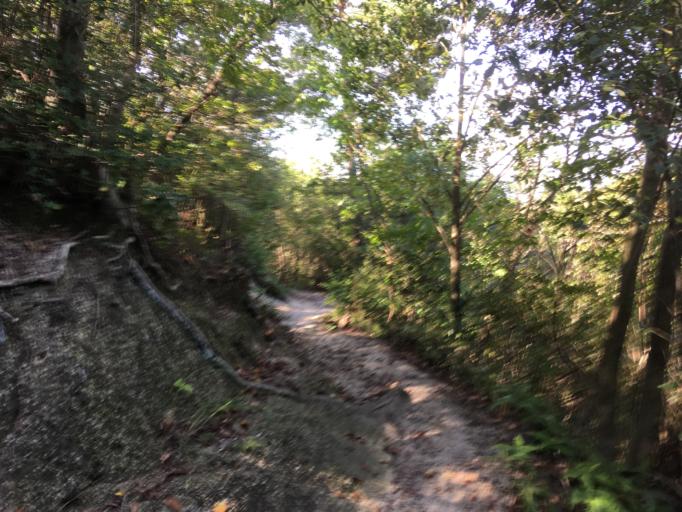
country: JP
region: Osaka
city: Neyagawa
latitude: 34.7464
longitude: 135.6828
